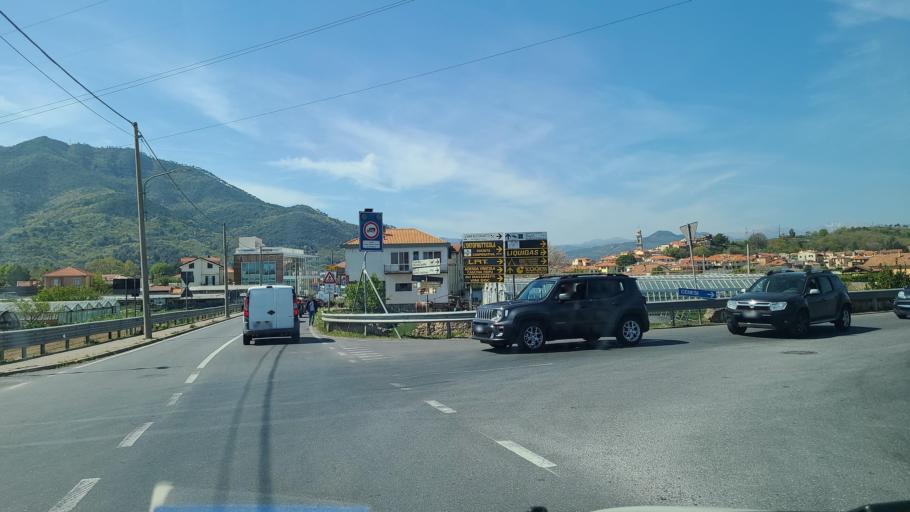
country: IT
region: Liguria
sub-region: Provincia di Savona
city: San Fedele-Lusignano
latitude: 44.0588
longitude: 8.1793
